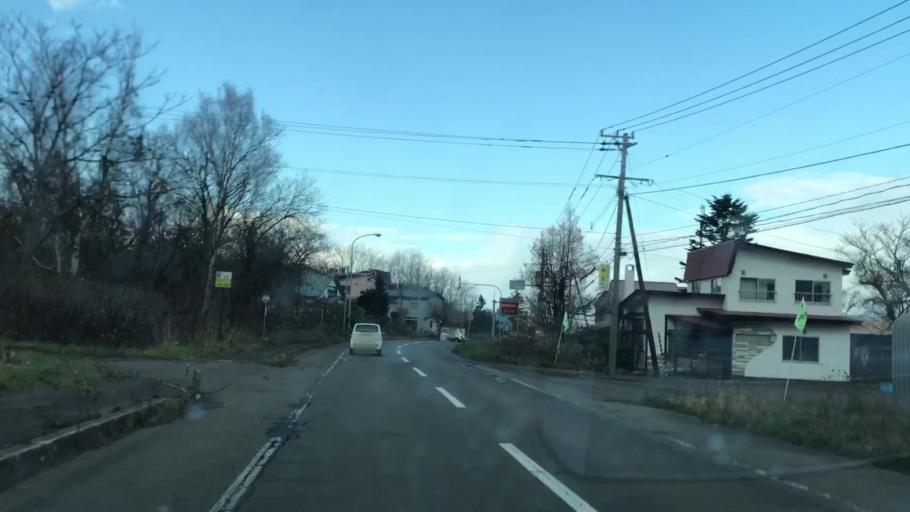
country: JP
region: Hokkaido
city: Yoichi
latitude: 43.3385
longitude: 140.4600
